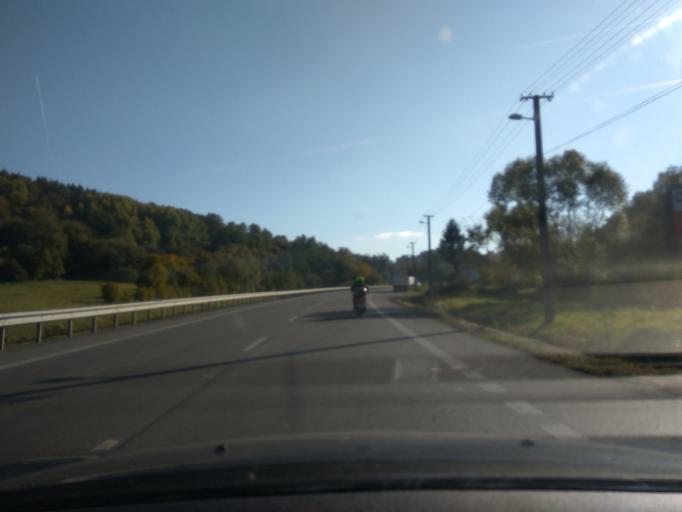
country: SK
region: Nitriansky
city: Handlova
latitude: 48.7442
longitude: 18.7650
